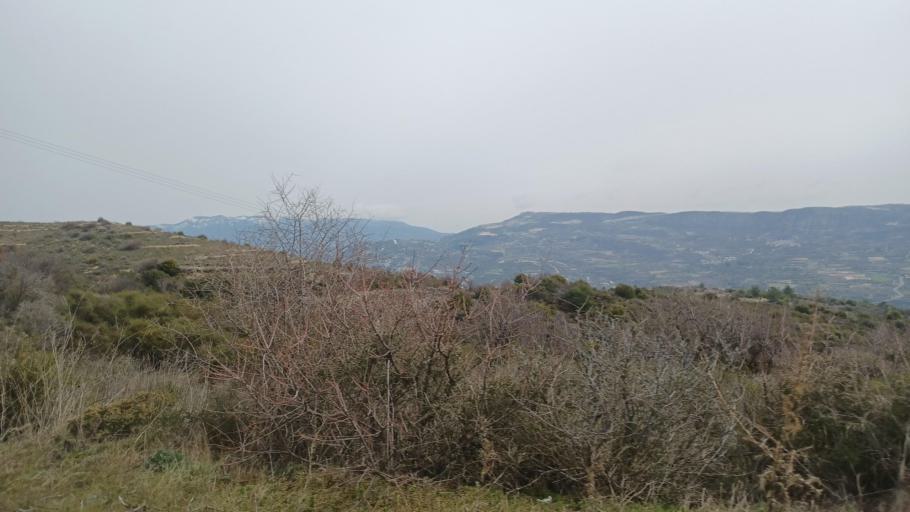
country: CY
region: Limassol
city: Pachna
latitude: 34.8585
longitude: 32.7024
